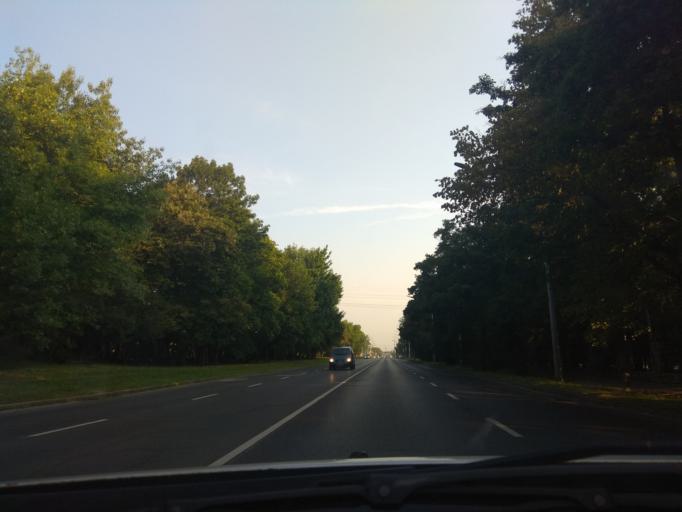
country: HU
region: Borsod-Abauj-Zemplen
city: Miskolc
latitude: 48.1225
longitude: 20.7867
